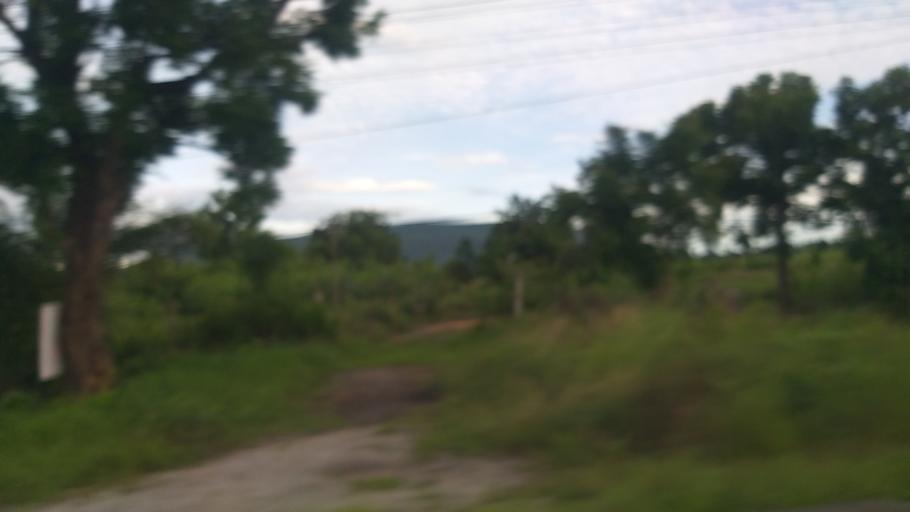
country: TH
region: Chaiyaphum
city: Phu Khiao
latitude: 16.2824
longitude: 102.2079
